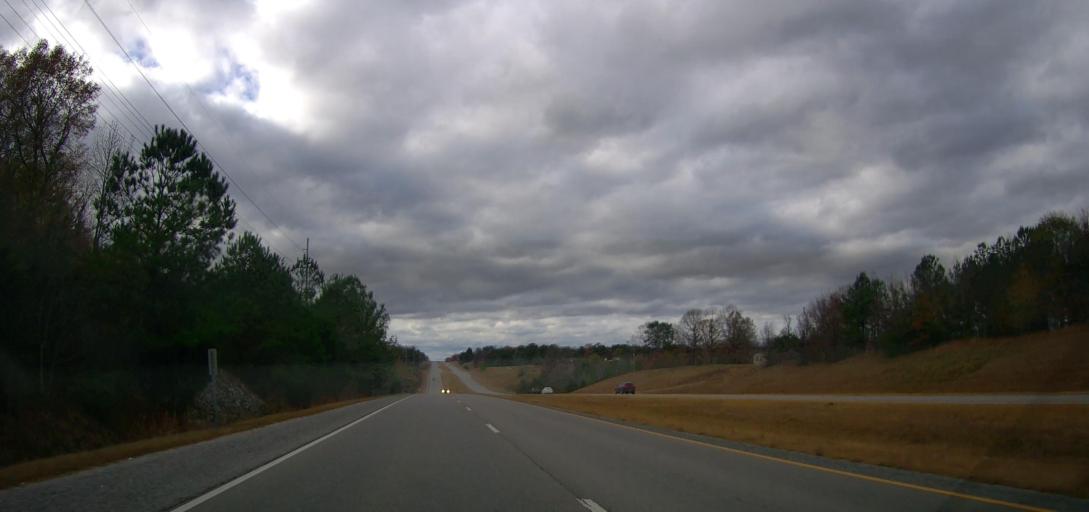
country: US
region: Alabama
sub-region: Lawrence County
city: Moulton
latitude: 34.5627
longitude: -87.3550
